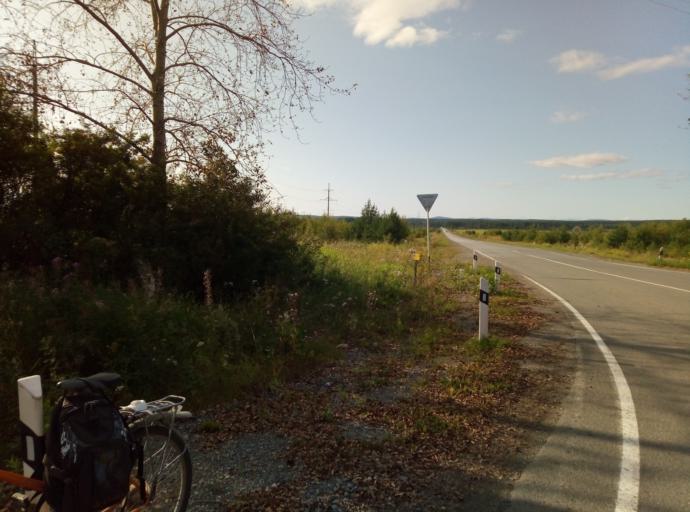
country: RU
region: Sverdlovsk
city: Karpinsk
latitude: 59.7893
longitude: 59.9929
